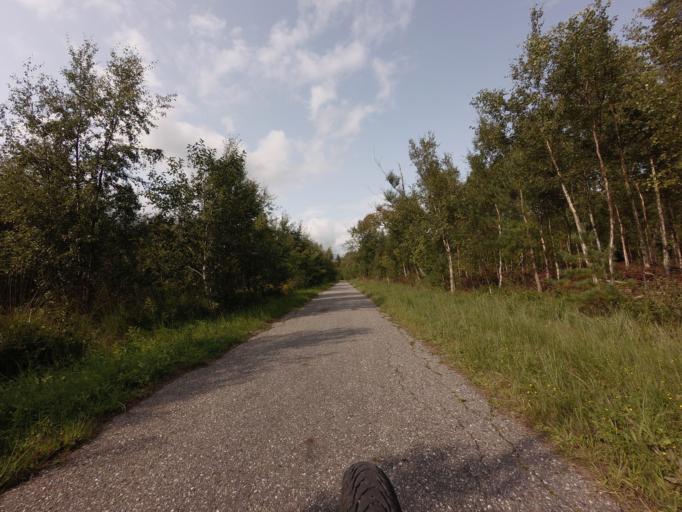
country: DK
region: North Denmark
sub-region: Frederikshavn Kommune
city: Skagen
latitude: 57.6398
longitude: 10.4551
